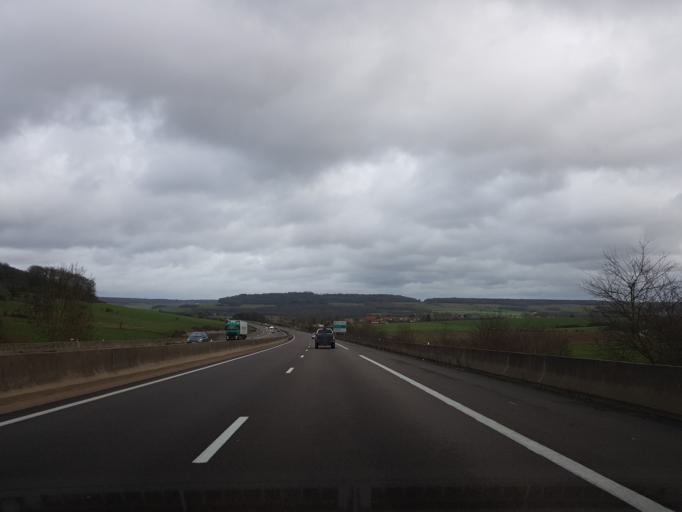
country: FR
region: Champagne-Ardenne
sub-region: Departement de la Haute-Marne
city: Rolampont
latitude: 47.9216
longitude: 5.2702
